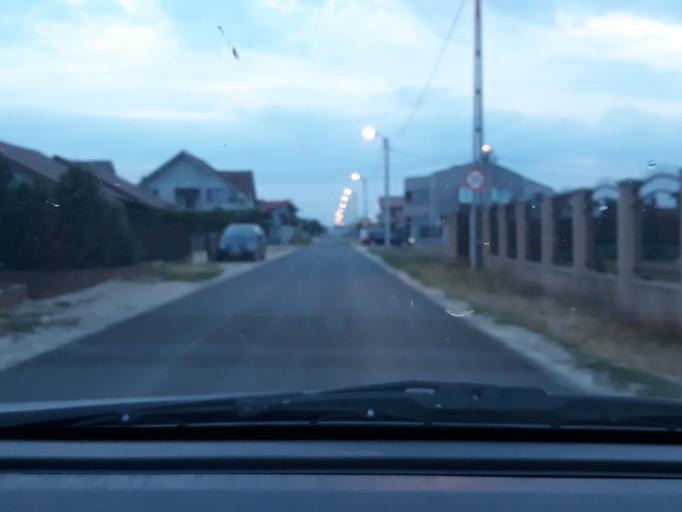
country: RO
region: Bihor
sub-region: Comuna Biharea
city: Oradea
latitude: 47.0262
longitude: 21.9304
